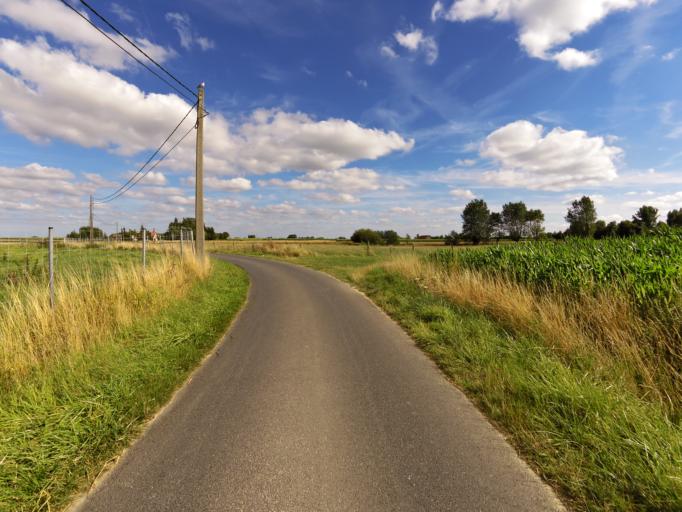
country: BE
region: Flanders
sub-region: Provincie West-Vlaanderen
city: Alveringem
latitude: 50.9797
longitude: 2.6634
